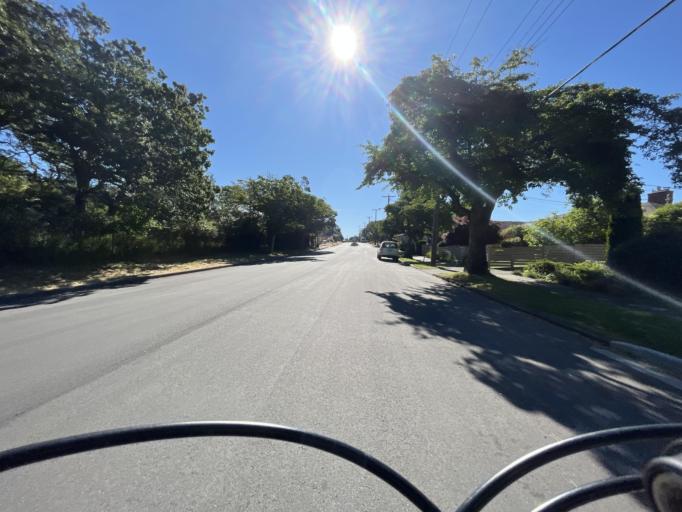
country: CA
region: British Columbia
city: Victoria
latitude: 48.4164
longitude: -123.3419
